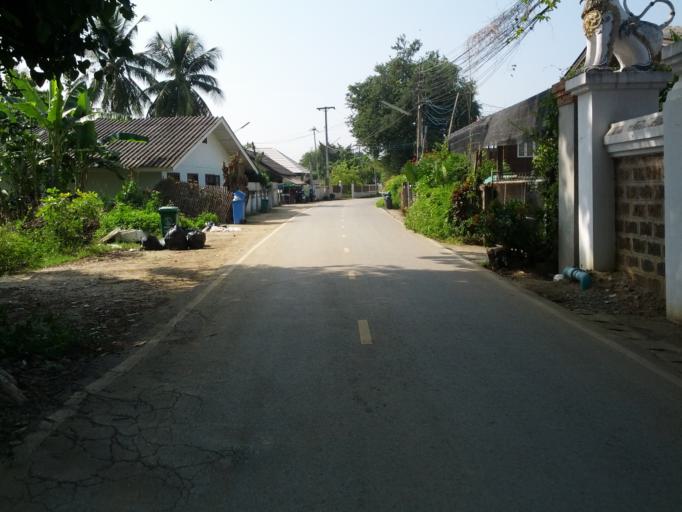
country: TH
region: Chiang Mai
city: San Kamphaeng
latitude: 18.7665
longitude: 99.0884
